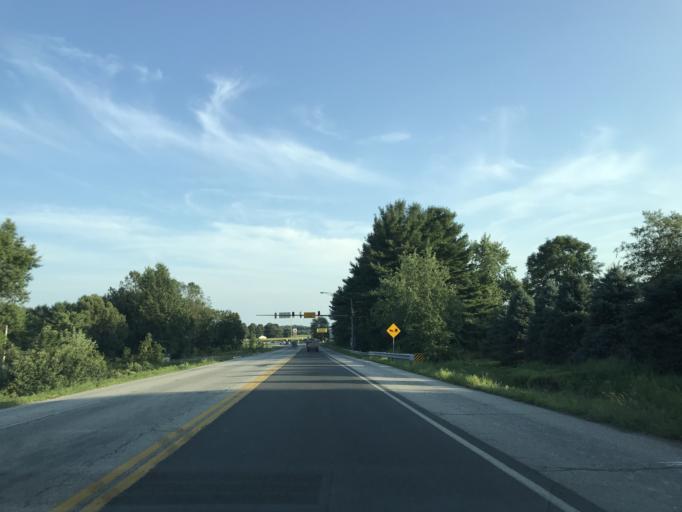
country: US
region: Maryland
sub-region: Cecil County
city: Rising Sun
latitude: 39.7000
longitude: -75.9791
